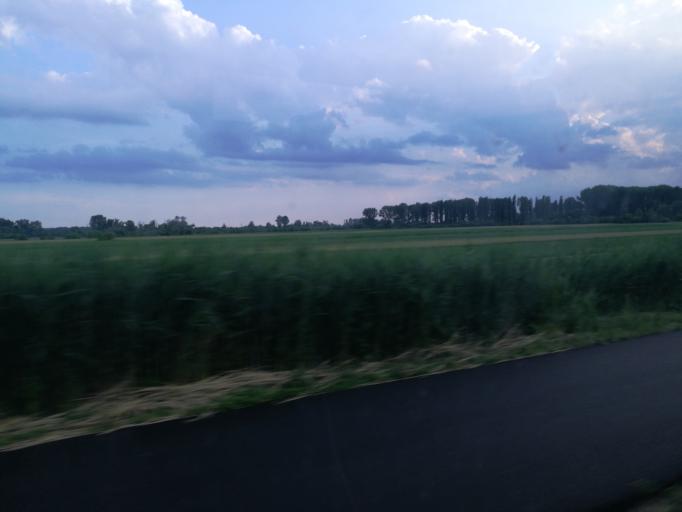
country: RO
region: Dambovita
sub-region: Comuna Branistea
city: Dambovicioara
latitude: 44.6641
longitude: 25.5493
